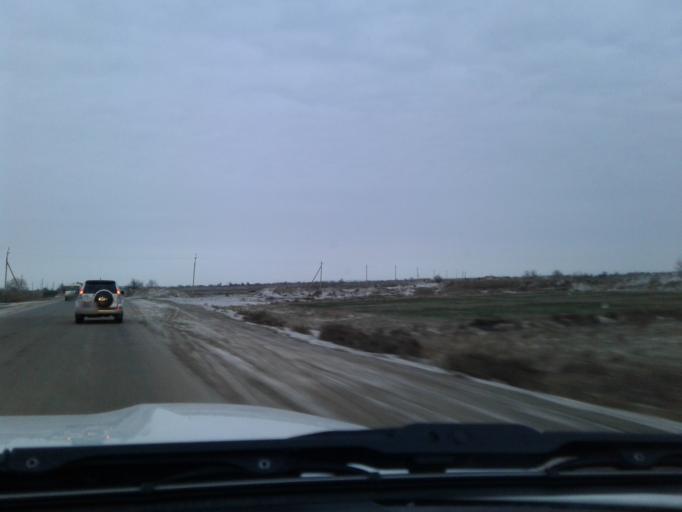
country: UZ
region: Karakalpakstan
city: Manghit
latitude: 42.0169
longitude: 59.8953
